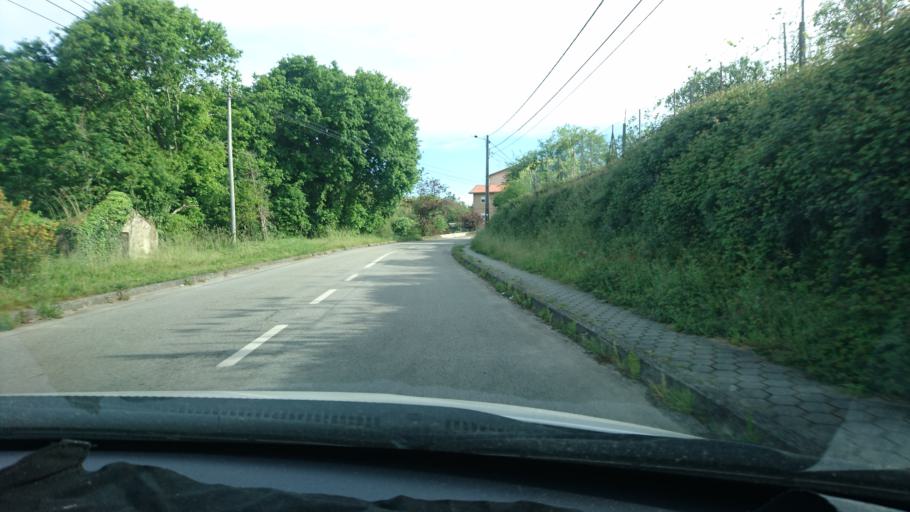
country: PT
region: Aveiro
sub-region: Oliveira de Azemeis
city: Sao Roque
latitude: 40.8763
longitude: -8.4859
